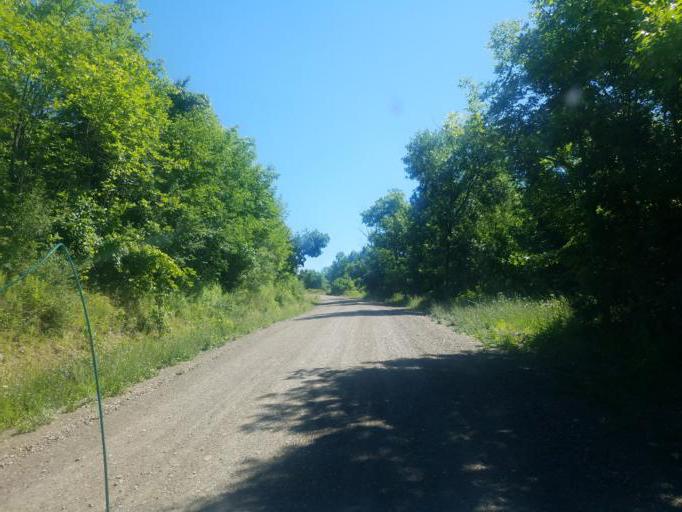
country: US
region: New York
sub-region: Ontario County
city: Naples
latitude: 42.6611
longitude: -77.3458
